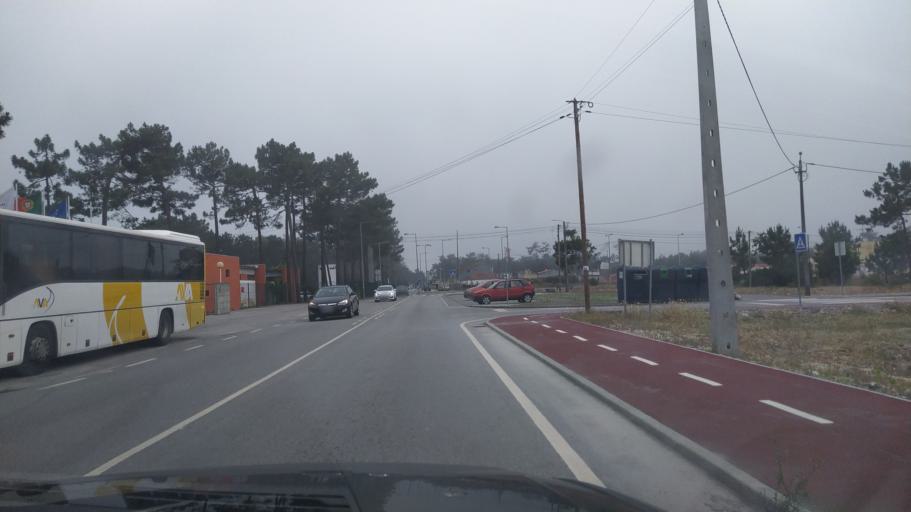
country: PT
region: Aveiro
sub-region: Ilhavo
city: Gafanha da Encarnacao
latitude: 40.5585
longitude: -8.7451
